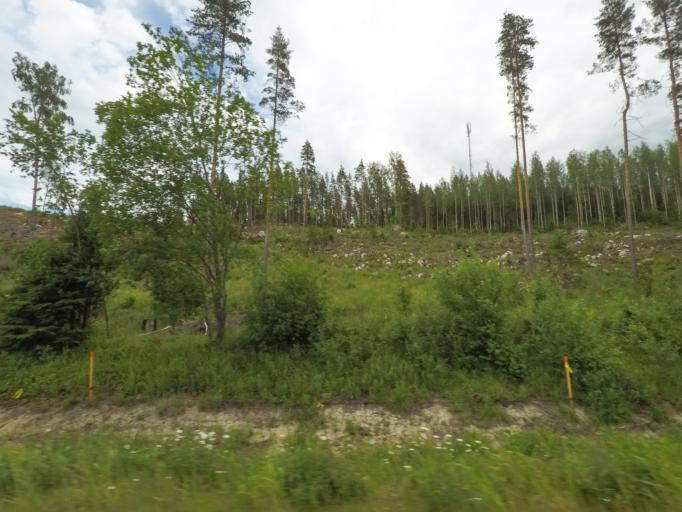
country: FI
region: Uusimaa
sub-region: Porvoo
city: Pukkila
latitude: 60.7978
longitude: 25.4708
